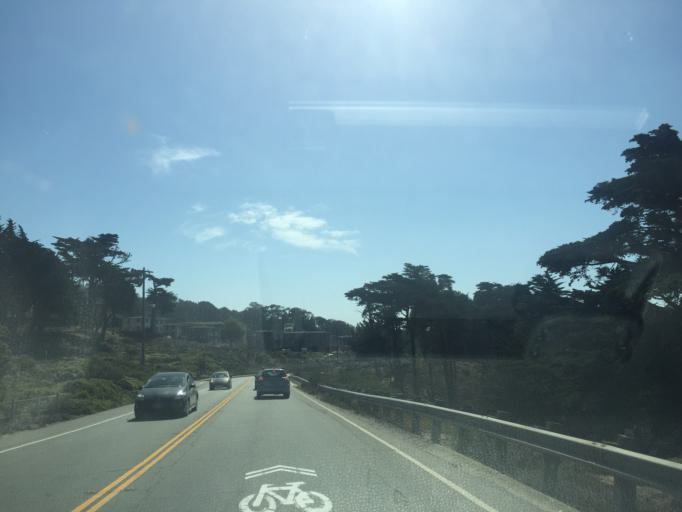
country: US
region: California
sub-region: Marin County
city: Sausalito
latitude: 37.7951
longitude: -122.4805
